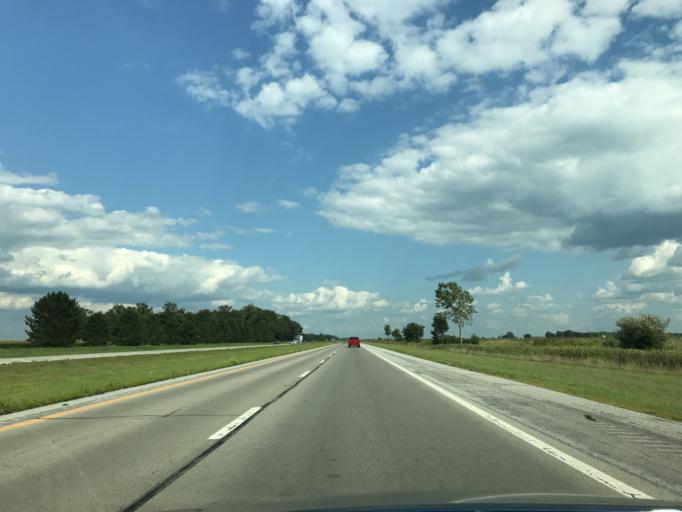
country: US
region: Ohio
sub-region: Allen County
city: Delphos
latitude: 40.8376
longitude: -84.2746
